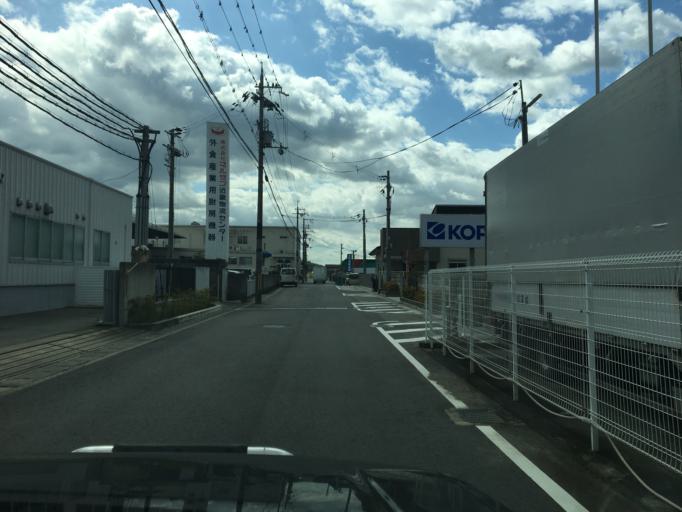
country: JP
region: Kyoto
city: Tanabe
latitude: 34.8174
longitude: 135.7908
